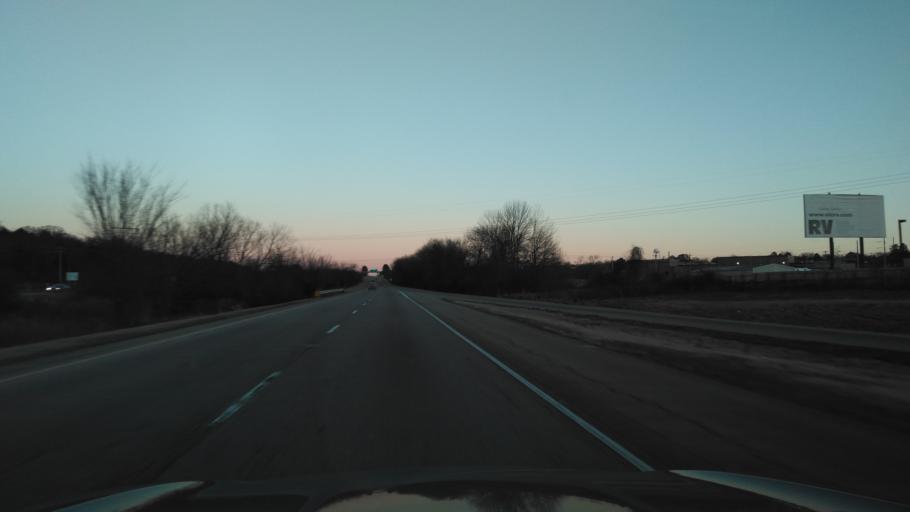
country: US
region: Arkansas
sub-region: Crawford County
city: Van Buren
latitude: 35.4622
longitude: -94.3542
